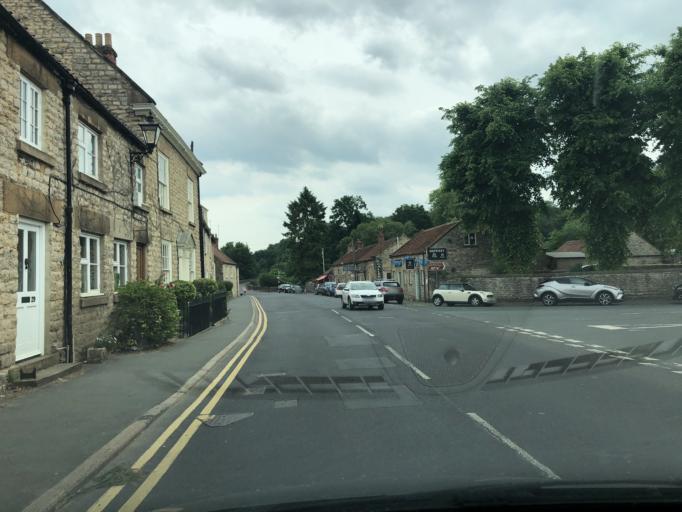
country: GB
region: England
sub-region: North Yorkshire
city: Helmsley
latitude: 54.2454
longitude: -1.0603
